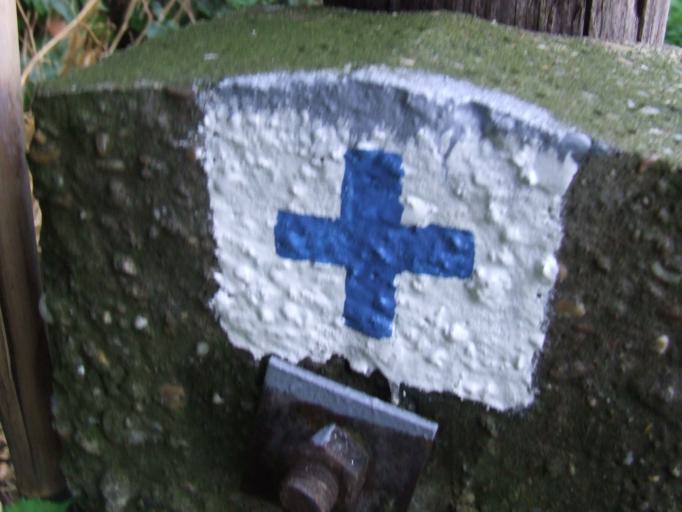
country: HU
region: Somogy
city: Kaposvar
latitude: 46.3130
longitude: 17.8016
